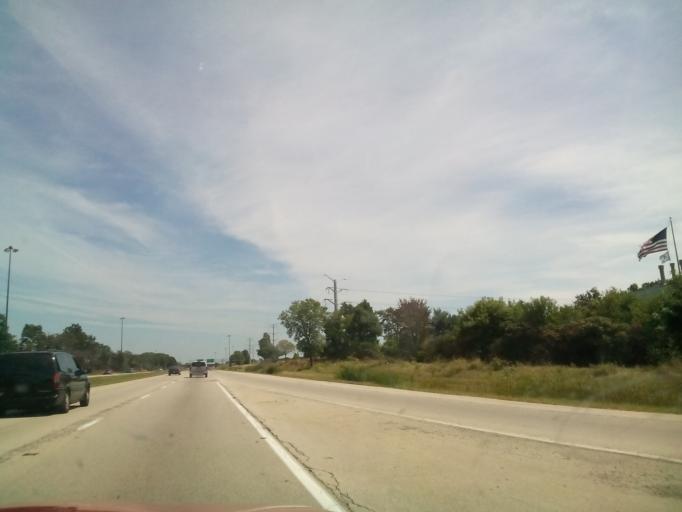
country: US
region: Illinois
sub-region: Winnebago County
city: Cherry Valley
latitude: 42.2199
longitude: -89.0256
